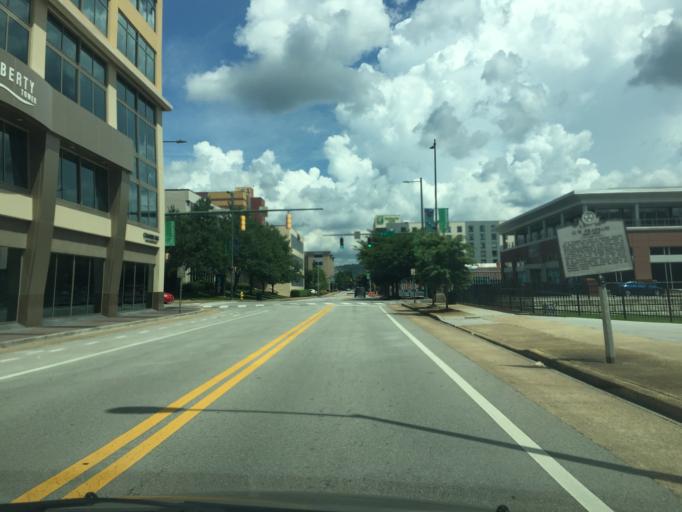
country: US
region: Tennessee
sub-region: Hamilton County
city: Chattanooga
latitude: 35.0491
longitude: -85.3117
